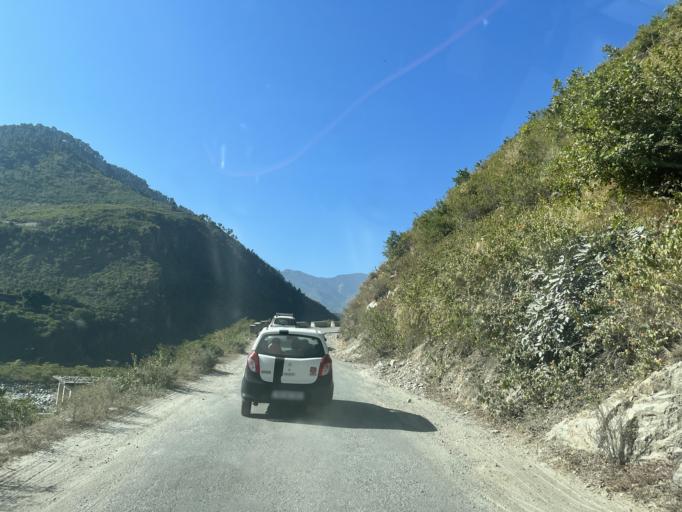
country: IN
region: Uttarakhand
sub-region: Naini Tal
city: Naini Tal
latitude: 29.5115
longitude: 79.4745
